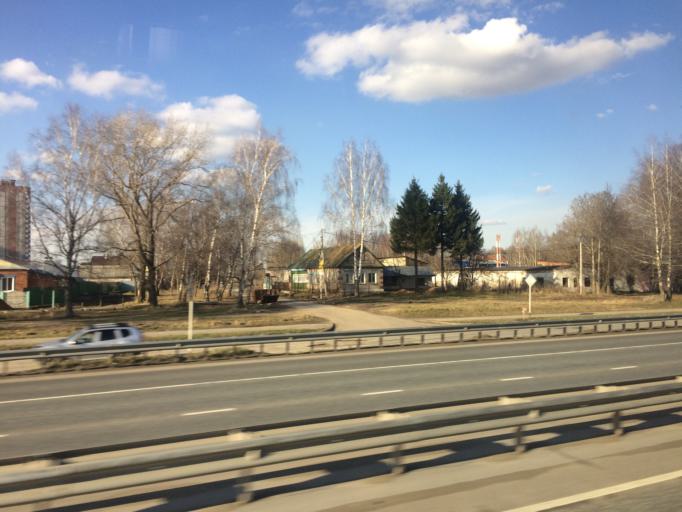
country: RU
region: Tatarstan
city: Osinovo
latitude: 55.8489
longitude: 48.9021
